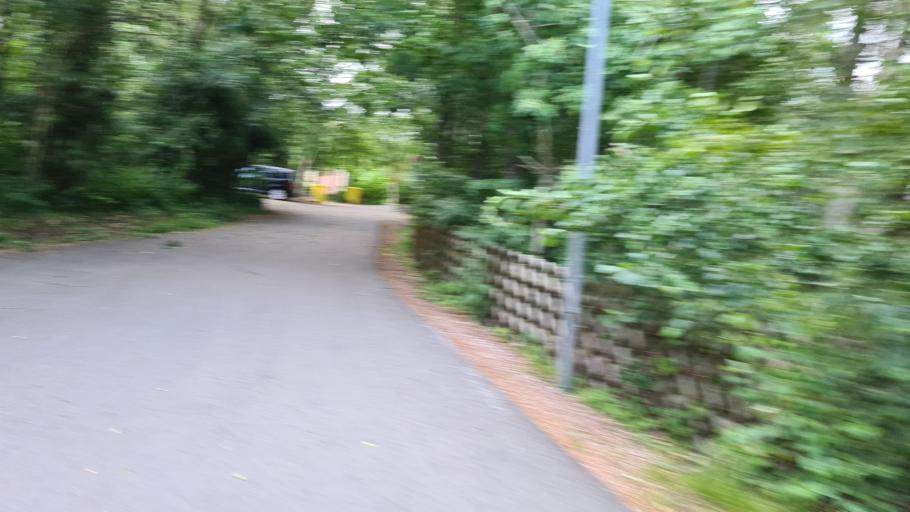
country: DE
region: Schleswig-Holstein
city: Sankt Peter-Ording
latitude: 54.2911
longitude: 8.6492
